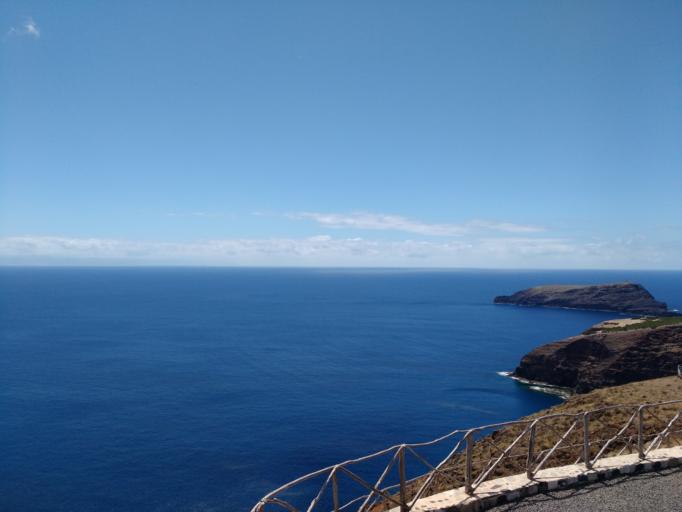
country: PT
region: Madeira
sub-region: Porto Santo
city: Vila de Porto Santo
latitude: 33.0289
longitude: -16.3813
